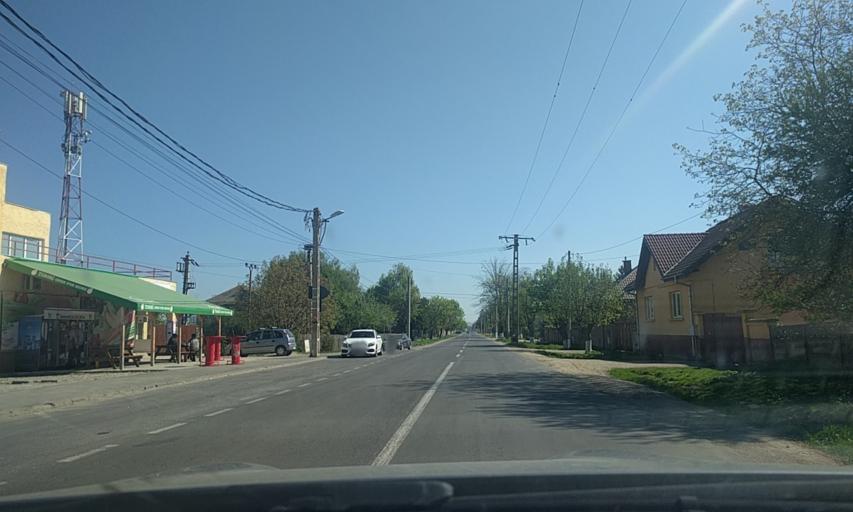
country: RO
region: Brasov
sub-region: Comuna Ghimbav
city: Ghimbav
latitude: 45.6983
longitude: 25.5584
